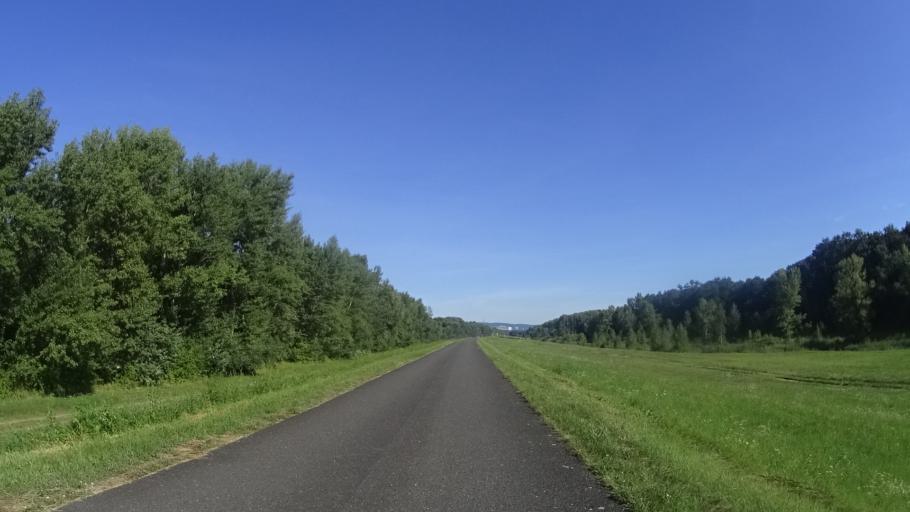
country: AT
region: Burgenland
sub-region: Politischer Bezirk Neusiedl am See
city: Deutsch Jahrndorf
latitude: 48.0792
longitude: 17.1606
